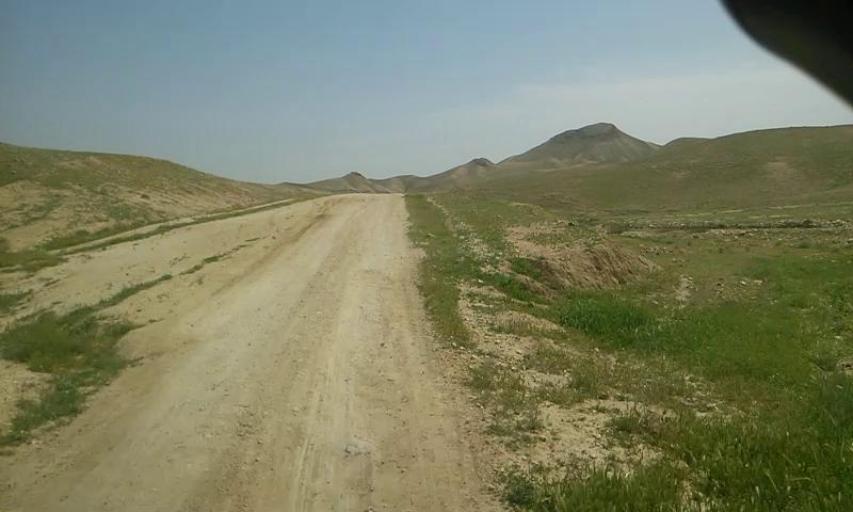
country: PS
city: `Arab ar Rashaydah
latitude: 31.5085
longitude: 35.2833
